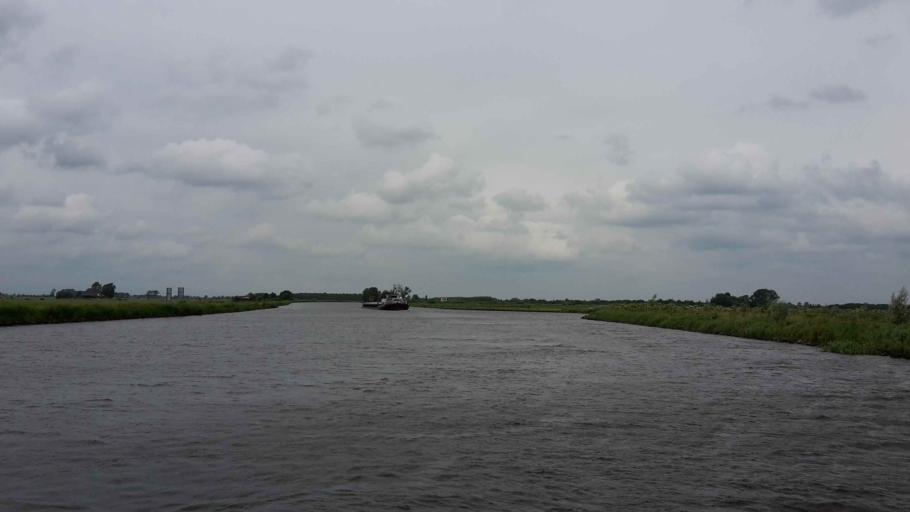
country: NL
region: Friesland
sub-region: Gemeente Boarnsterhim
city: Warten
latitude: 53.1159
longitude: 5.8762
